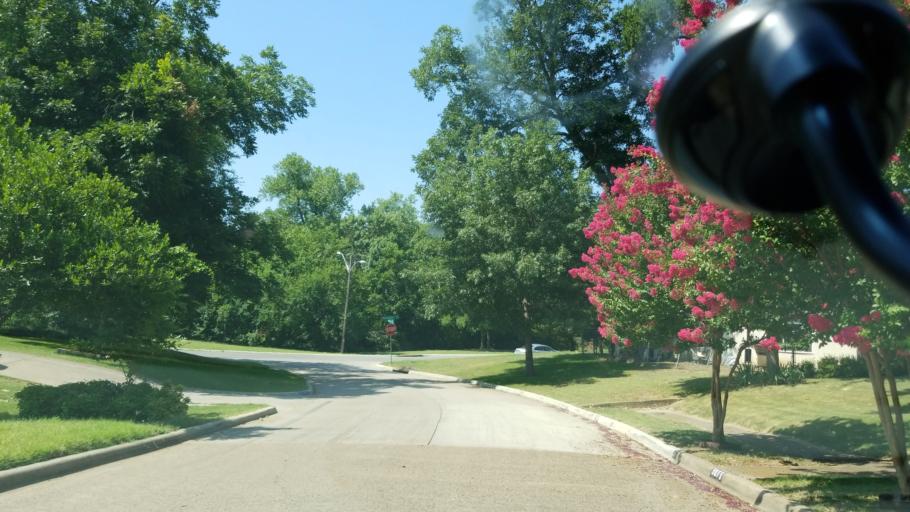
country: US
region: Texas
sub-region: Dallas County
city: Cockrell Hill
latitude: 32.7085
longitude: -96.8783
